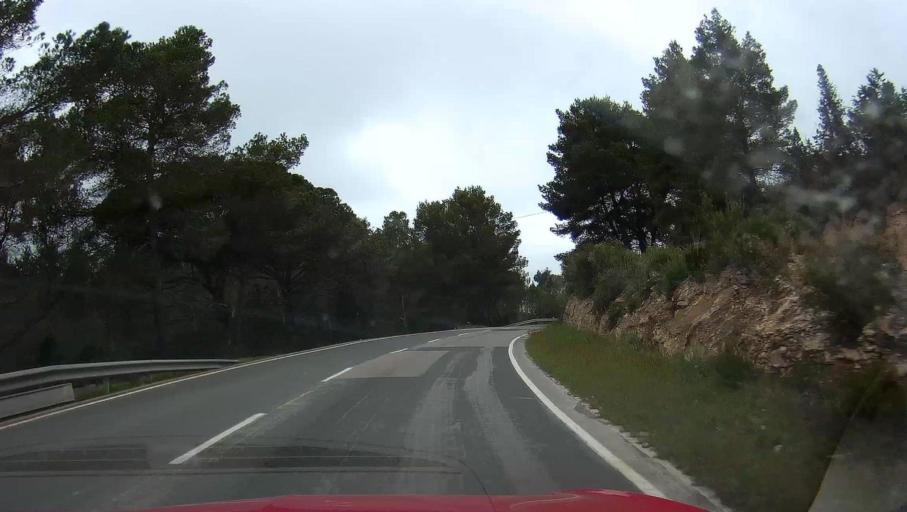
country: ES
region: Balearic Islands
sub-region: Illes Balears
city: Sant Joan de Labritja
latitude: 39.0776
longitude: 1.5023
